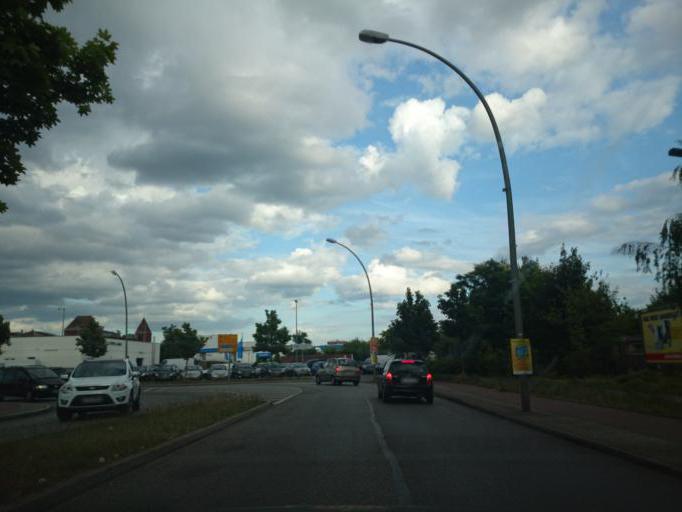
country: DE
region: Berlin
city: Niederschoneweide
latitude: 52.4605
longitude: 13.5023
